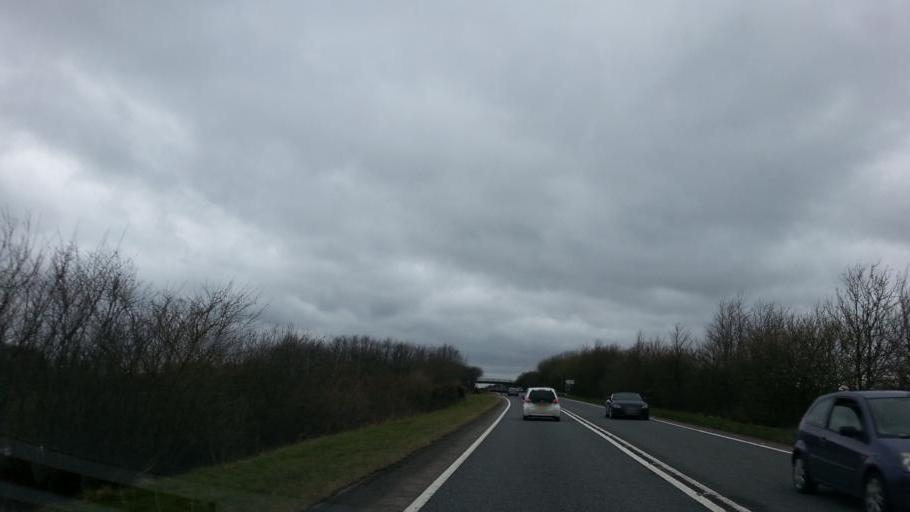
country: GB
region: England
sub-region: Devon
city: Tiverton
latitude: 50.9470
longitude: -3.5969
